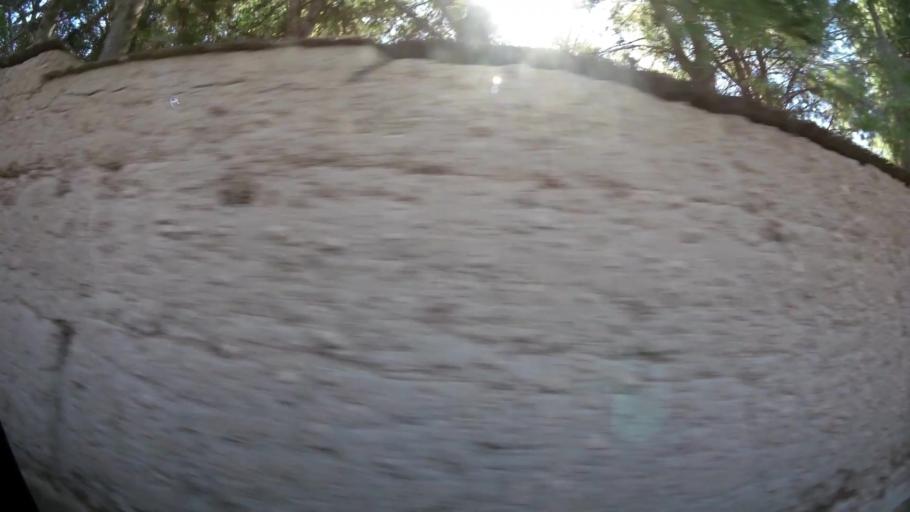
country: MA
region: Marrakech-Tensift-Al Haouz
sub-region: Marrakech
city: Marrakesh
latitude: 31.6673
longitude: -7.9599
